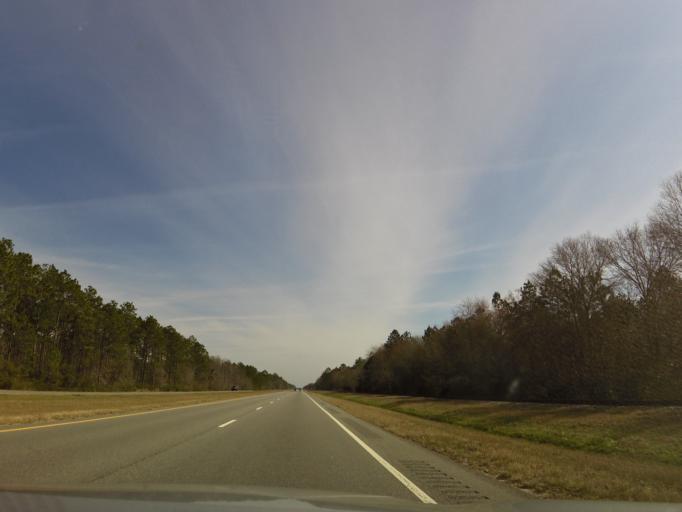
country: US
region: Georgia
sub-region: Lowndes County
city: Valdosta
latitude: 30.8804
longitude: -83.1496
